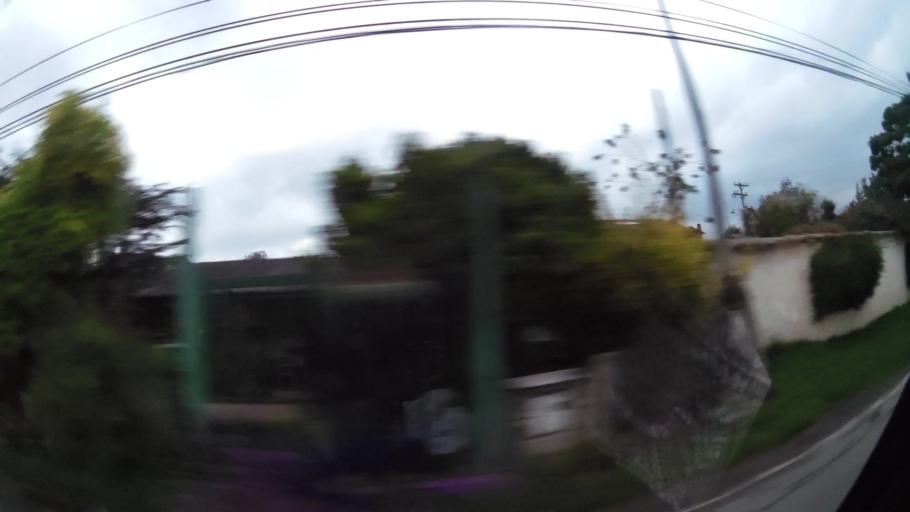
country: CO
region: Cundinamarca
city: Chia
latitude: 4.8396
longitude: -74.0716
